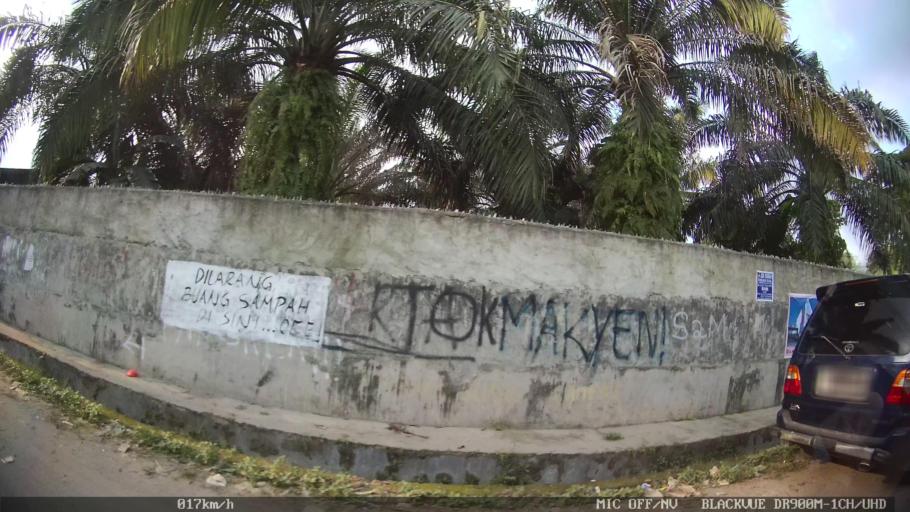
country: ID
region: North Sumatra
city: Medan
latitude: 3.5849
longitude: 98.7326
